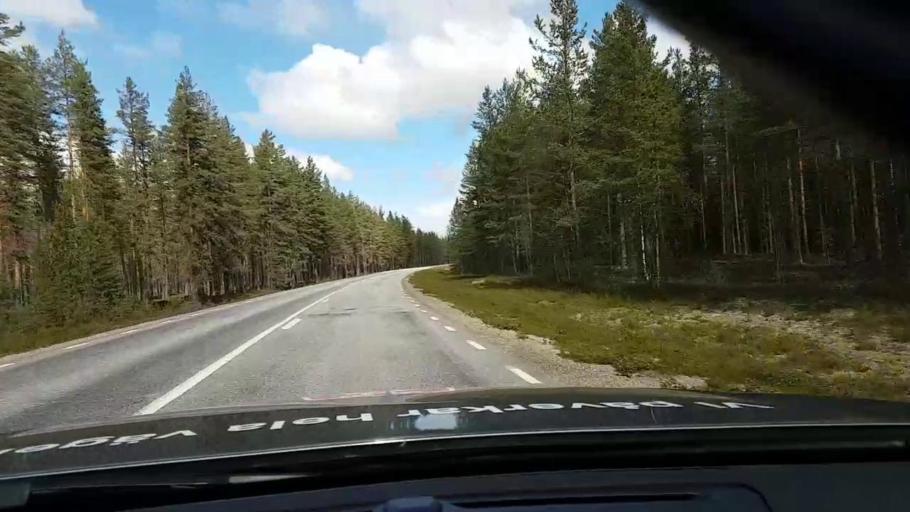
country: SE
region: Vaesternorrland
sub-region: OErnskoeldsviks Kommun
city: Bredbyn
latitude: 63.6093
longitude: 17.8999
